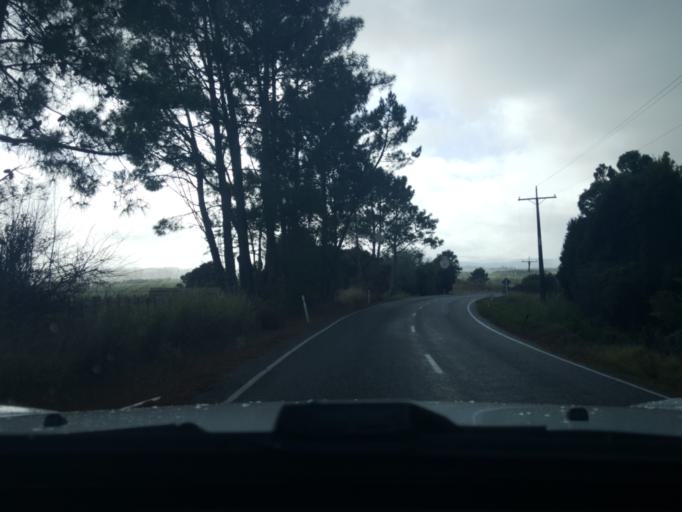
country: NZ
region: Waikato
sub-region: Waikato District
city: Te Kauwhata
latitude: -37.4449
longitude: 175.0837
